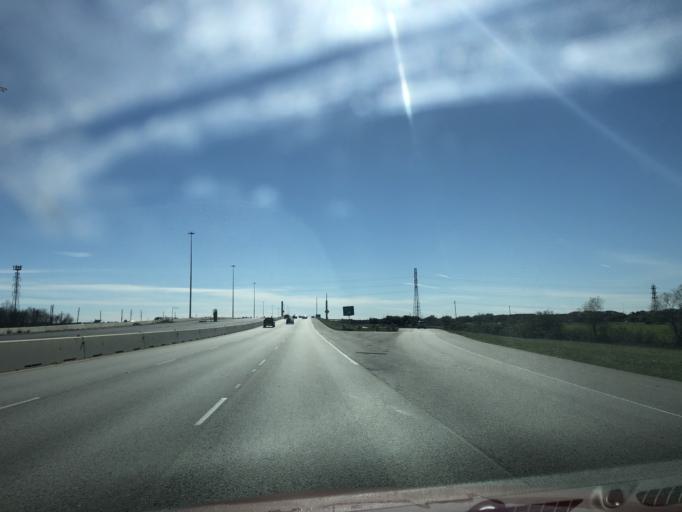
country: US
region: Texas
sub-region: Brazoria County
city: Brookside Village
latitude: 29.6315
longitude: -95.3873
